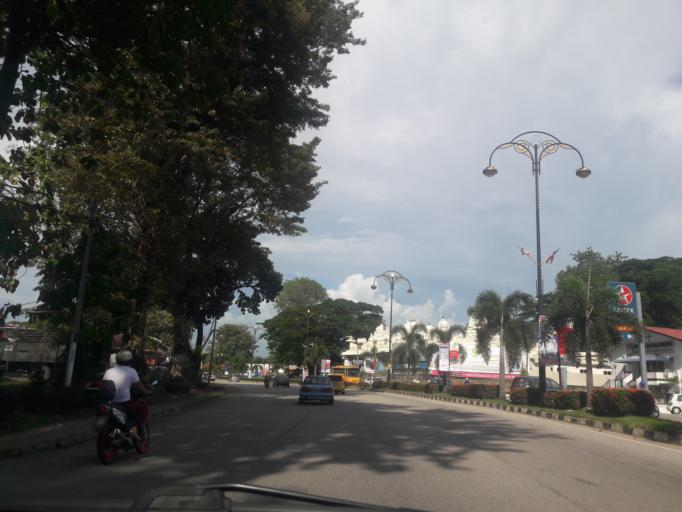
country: MY
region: Kedah
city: Sungai Petani
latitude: 5.6460
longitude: 100.4943
